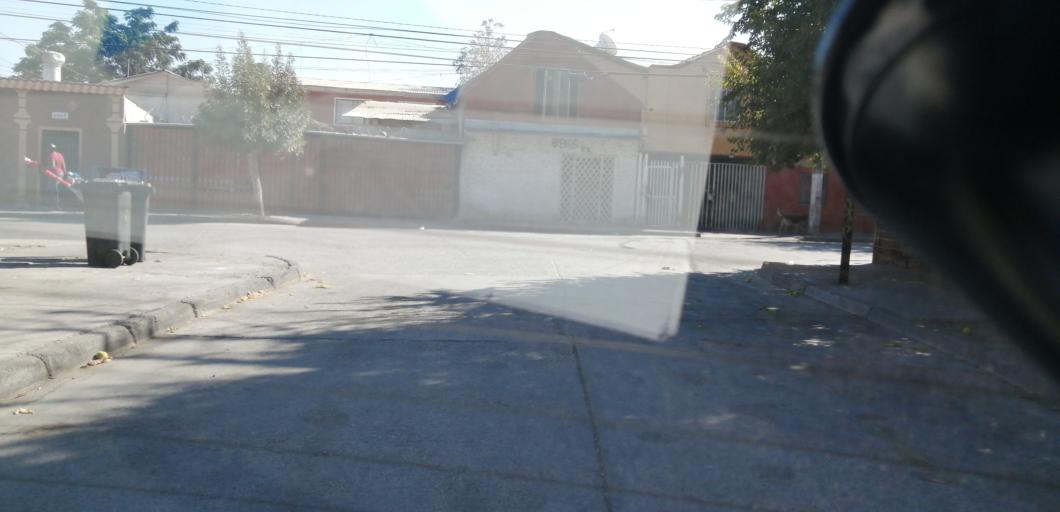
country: CL
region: Santiago Metropolitan
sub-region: Provincia de Santiago
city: Lo Prado
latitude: -33.4406
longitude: -70.7561
